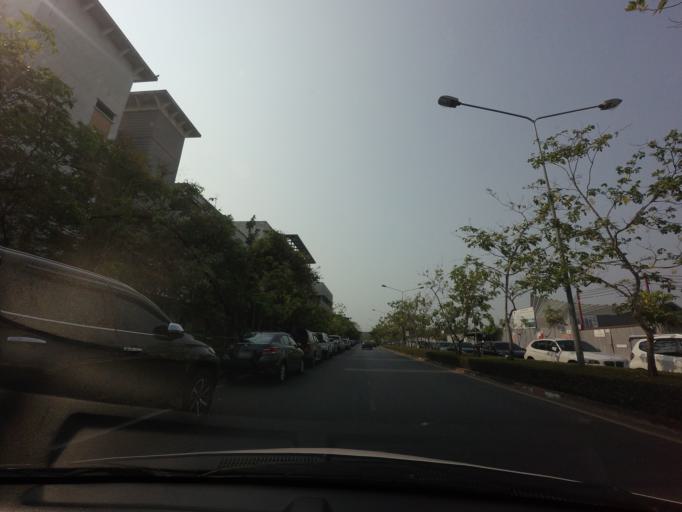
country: TH
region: Nakhon Pathom
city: Salaya
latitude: 13.7915
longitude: 100.3227
